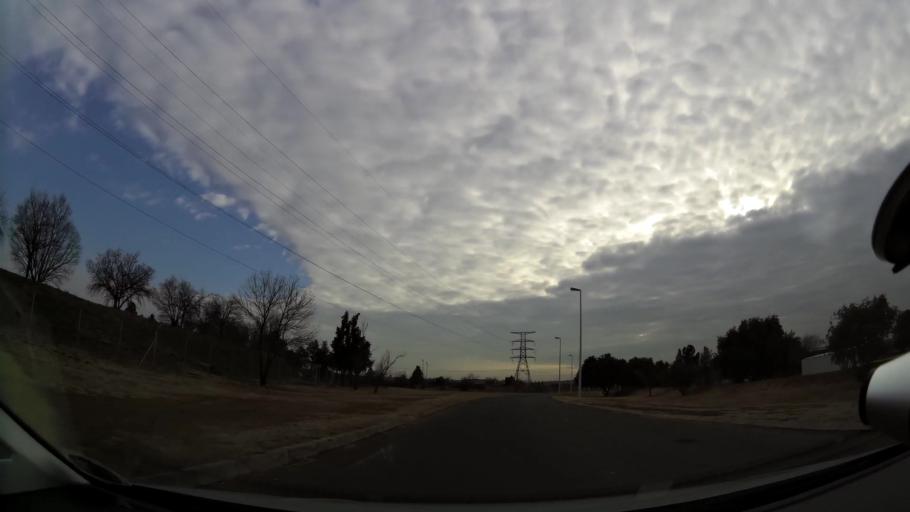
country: ZA
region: Orange Free State
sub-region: Mangaung Metropolitan Municipality
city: Bloemfontein
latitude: -29.1088
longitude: 26.1777
